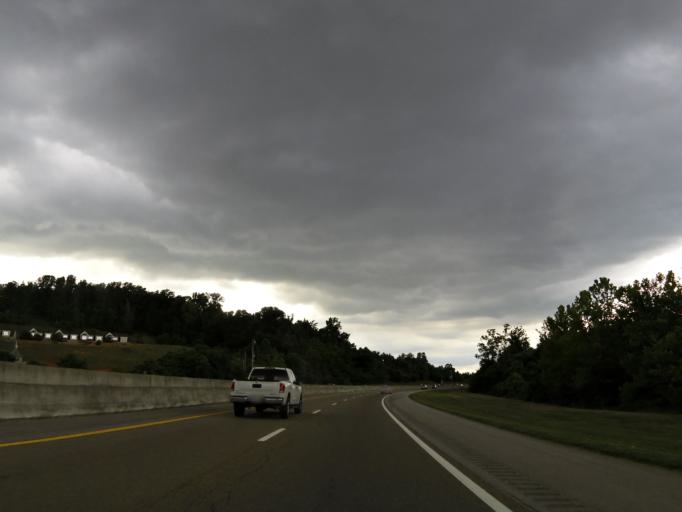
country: US
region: Tennessee
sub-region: Knox County
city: Farragut
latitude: 35.8920
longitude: -84.1130
